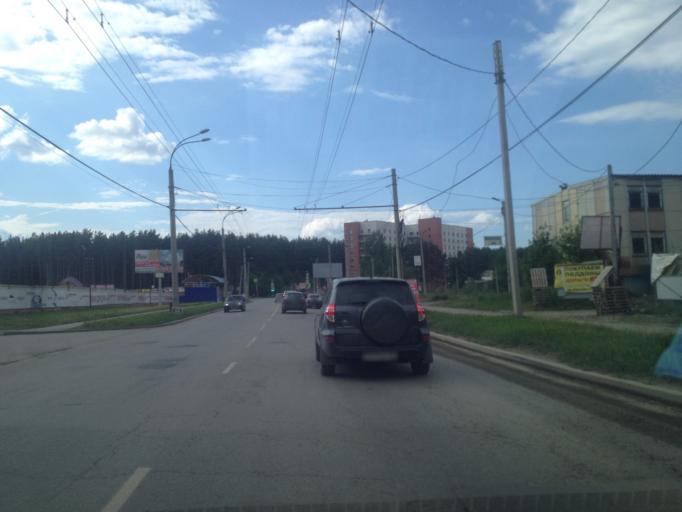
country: RU
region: Sverdlovsk
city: Sovkhoznyy
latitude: 56.7699
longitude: 60.5449
